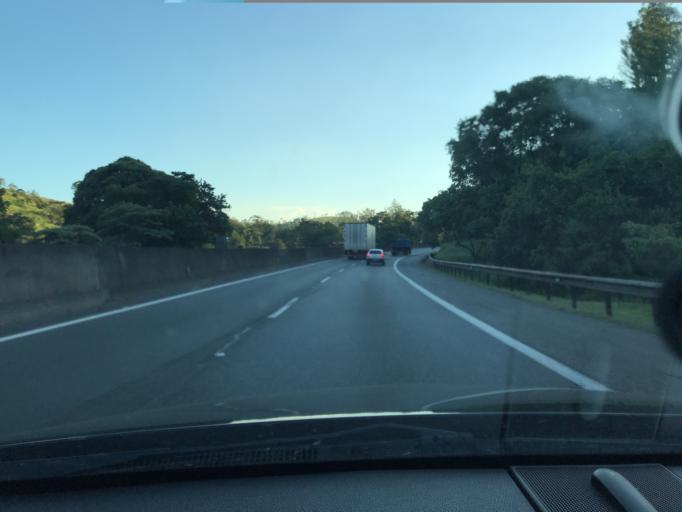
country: BR
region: Sao Paulo
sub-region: Cajamar
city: Cajamar
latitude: -23.3080
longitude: -46.8560
